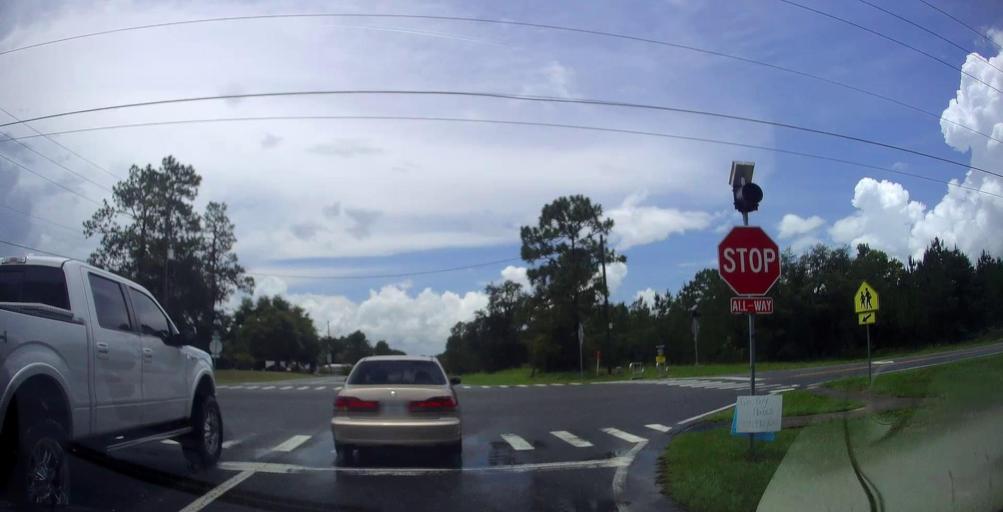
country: US
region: Florida
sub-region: Marion County
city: Silver Springs Shores
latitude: 29.1202
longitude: -82.0178
